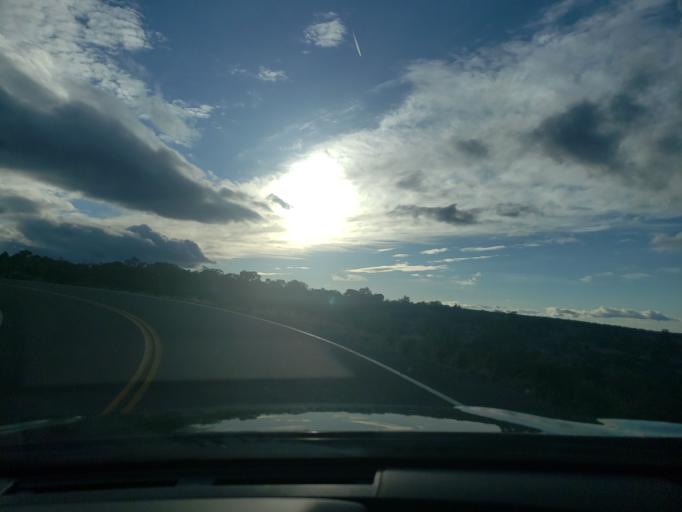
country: US
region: Colorado
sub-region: Mesa County
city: Redlands
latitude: 39.0335
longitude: -108.6499
